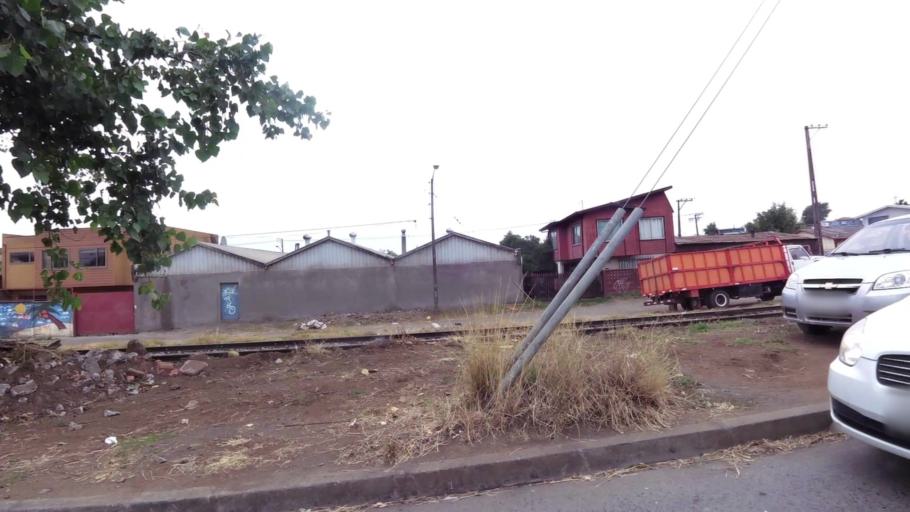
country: CL
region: Biobio
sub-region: Provincia de Concepcion
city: Concepcion
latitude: -36.8092
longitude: -73.0399
